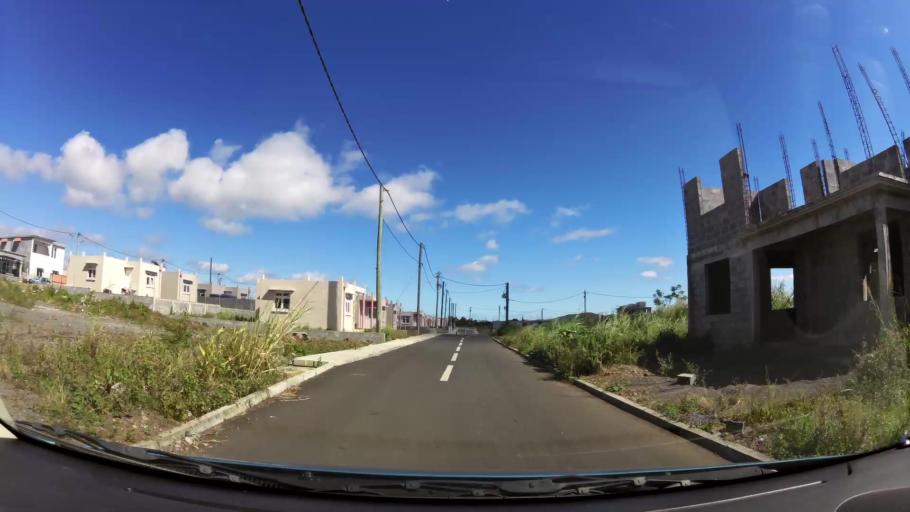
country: MU
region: Plaines Wilhems
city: Vacoas
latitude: -20.3286
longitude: 57.4830
